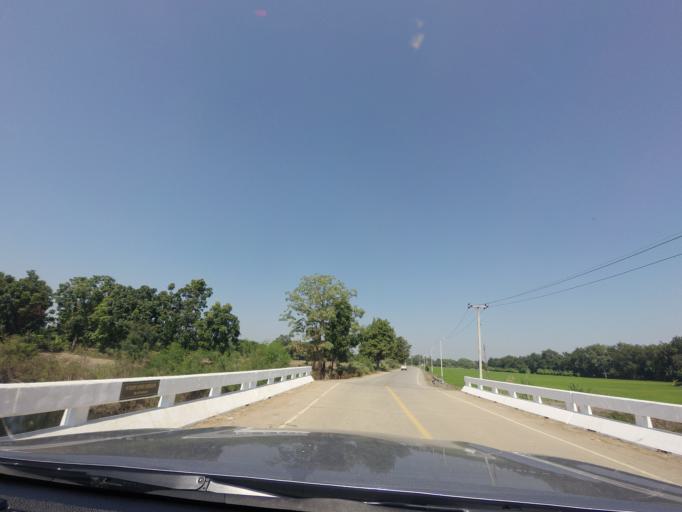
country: TH
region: Sukhothai
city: Si Samrong
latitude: 17.1595
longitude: 99.7702
